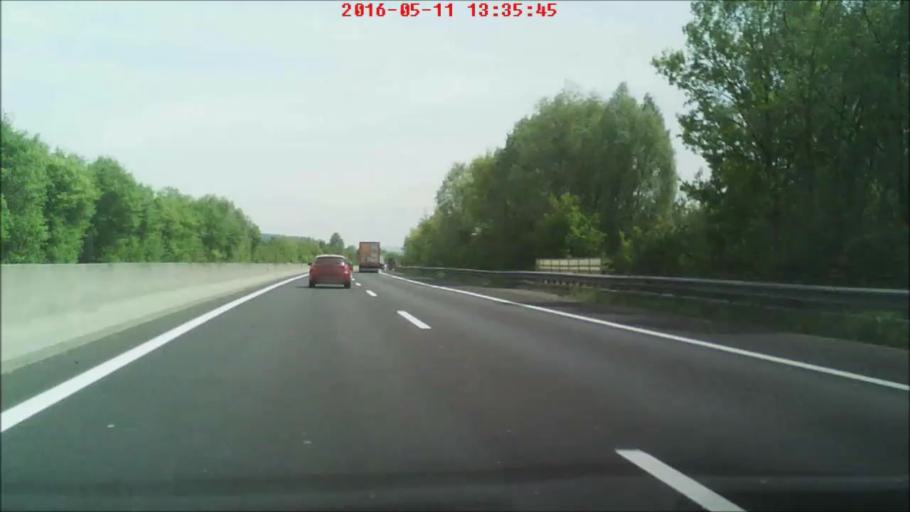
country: AT
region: Upper Austria
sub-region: Politischer Bezirk Ried im Innkreis
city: Ried im Innkreis
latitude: 48.2975
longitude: 13.4787
